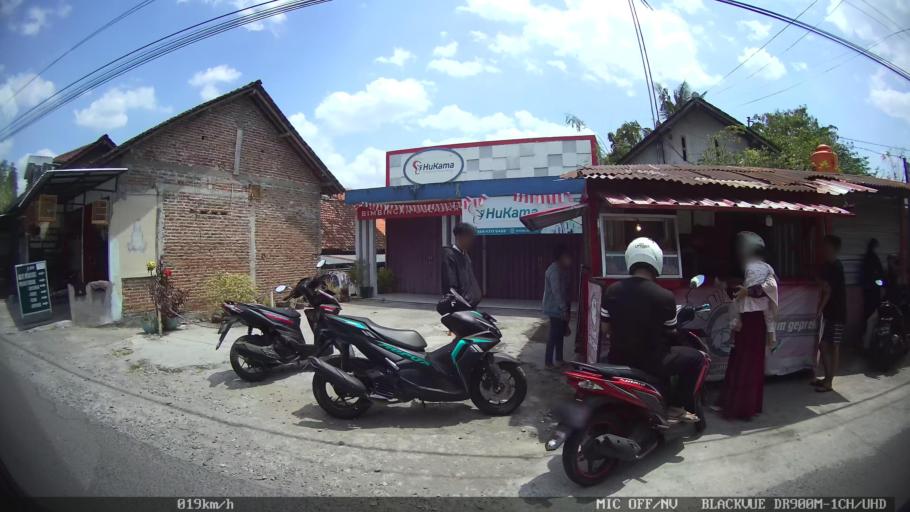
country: ID
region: Daerah Istimewa Yogyakarta
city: Kasihan
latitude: -7.8146
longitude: 110.3432
